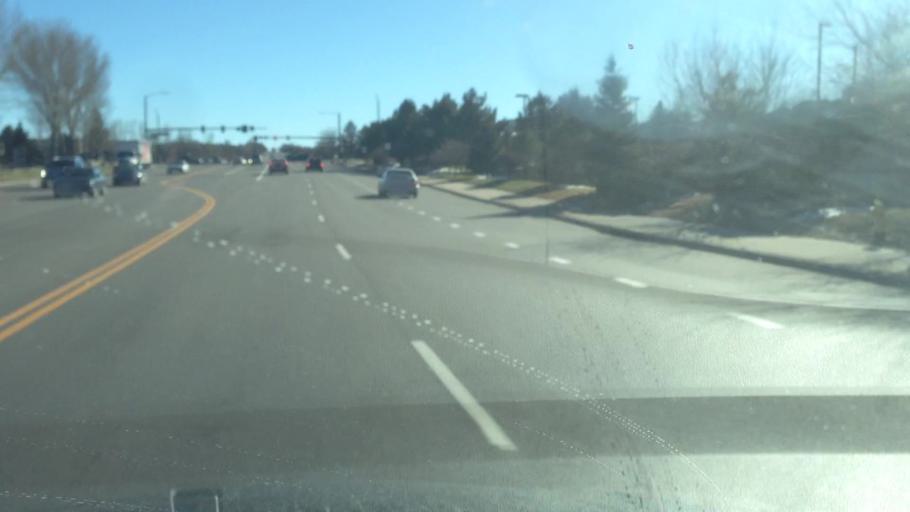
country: US
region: Colorado
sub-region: Douglas County
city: Stonegate
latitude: 39.5358
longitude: -104.7935
